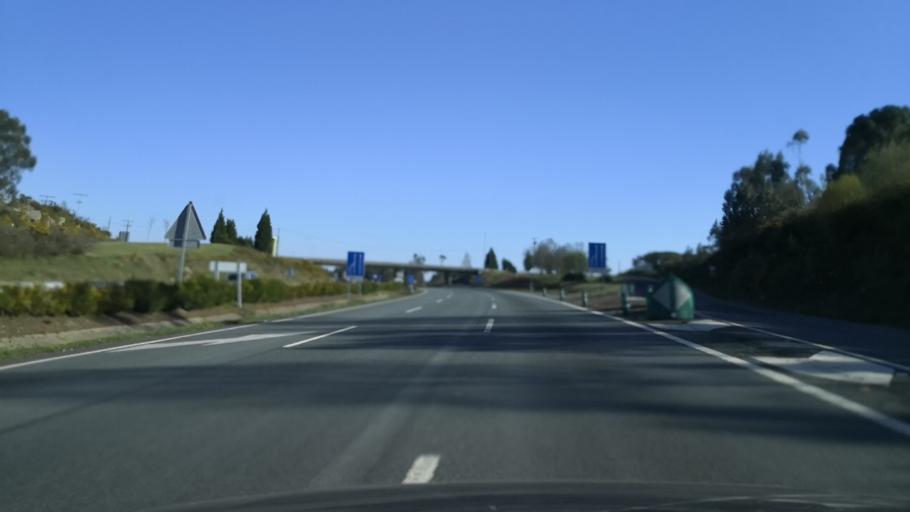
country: ES
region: Galicia
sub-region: Provincia da Coruna
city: Aranga
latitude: 43.2153
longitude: -8.0523
